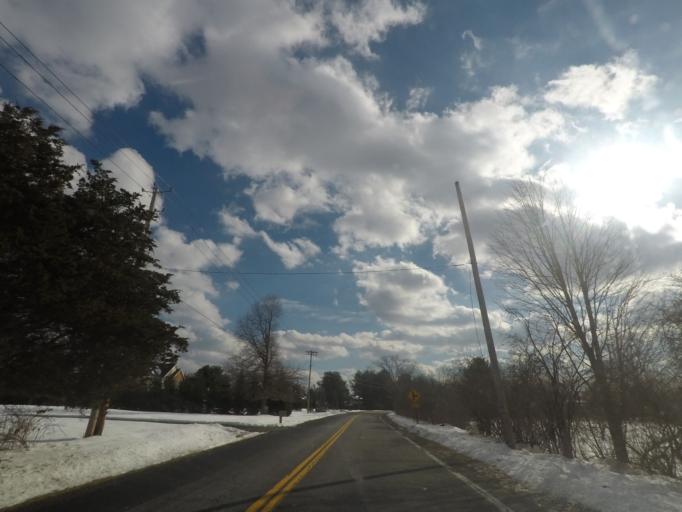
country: US
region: New York
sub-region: Schenectady County
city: Niskayuna
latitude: 42.8311
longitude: -73.8631
